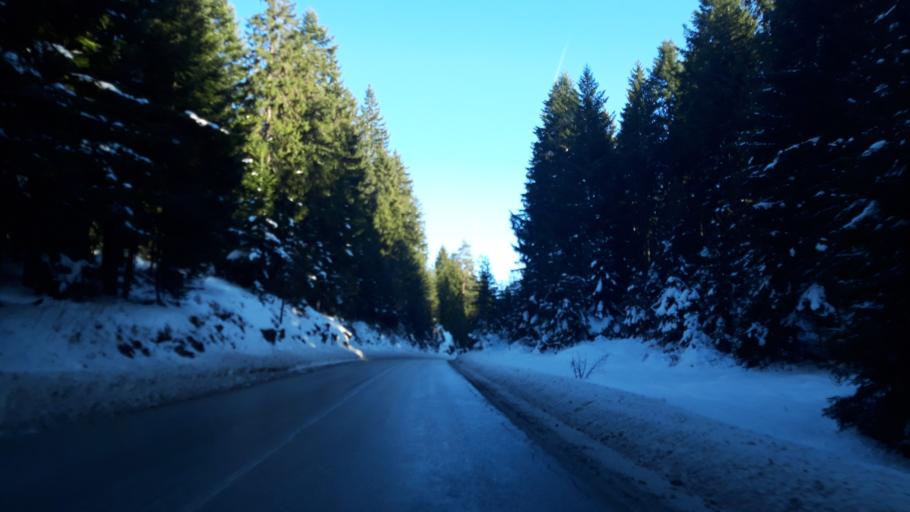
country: BA
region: Republika Srpska
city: Sokolac
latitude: 43.9259
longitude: 18.6659
